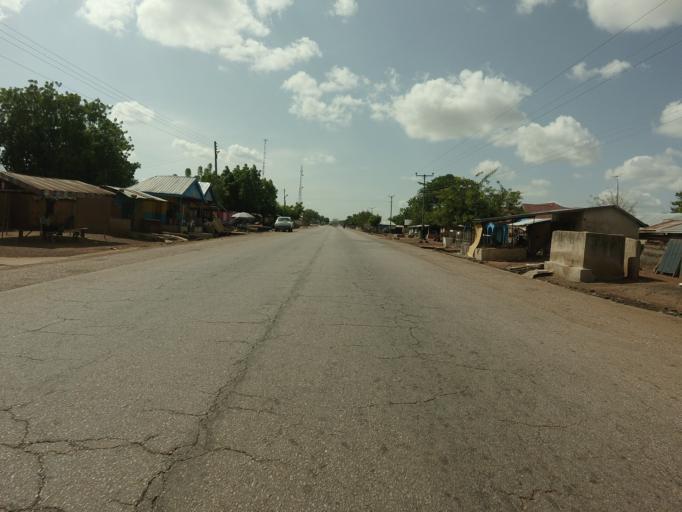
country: GH
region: Northern
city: Savelugu
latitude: 9.8689
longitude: -0.8714
